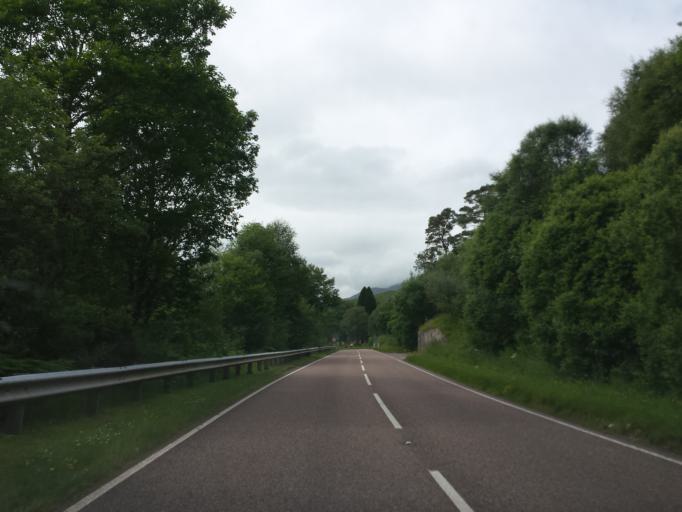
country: GB
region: Scotland
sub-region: Highland
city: Fort William
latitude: 56.8581
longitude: -5.3144
